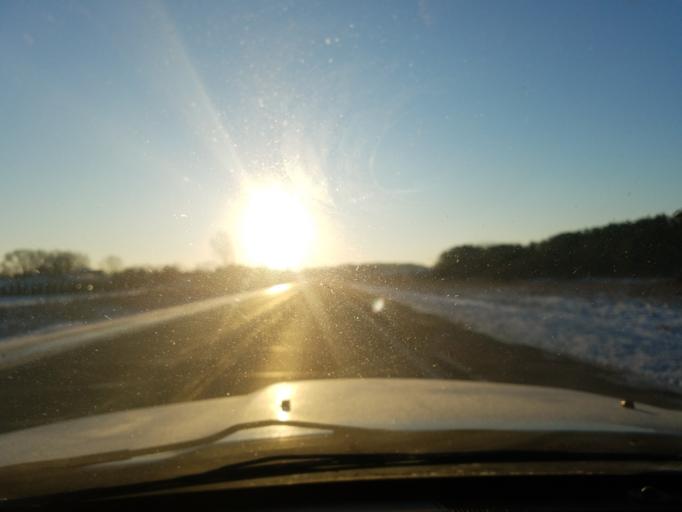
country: US
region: Indiana
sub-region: Marshall County
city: Bremen
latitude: 41.4584
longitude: -86.1388
